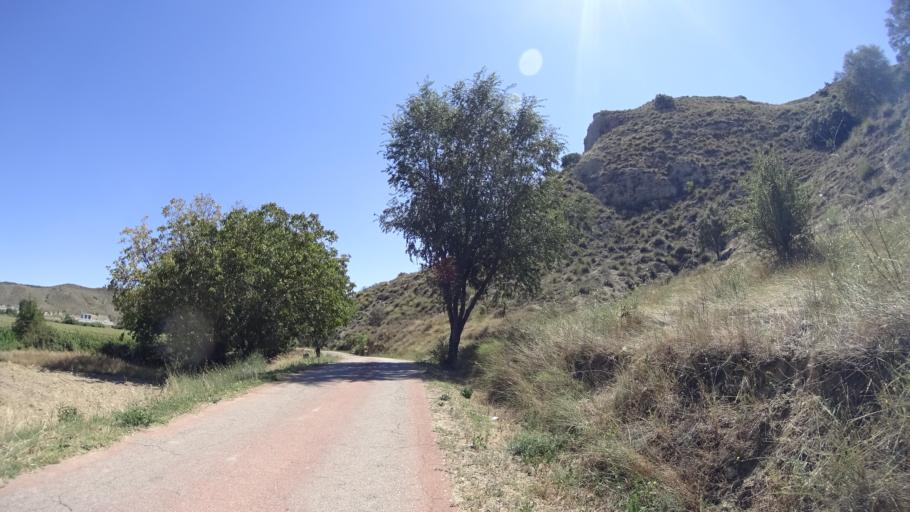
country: ES
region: Madrid
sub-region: Provincia de Madrid
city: Tielmes
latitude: 40.2410
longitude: -3.2986
